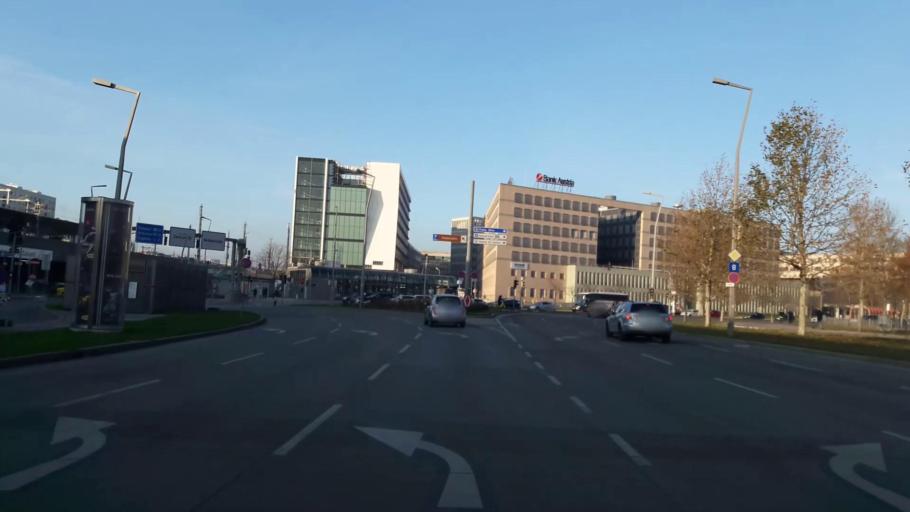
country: AT
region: Vienna
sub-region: Wien Stadt
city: Vienna
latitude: 48.2187
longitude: 16.3935
